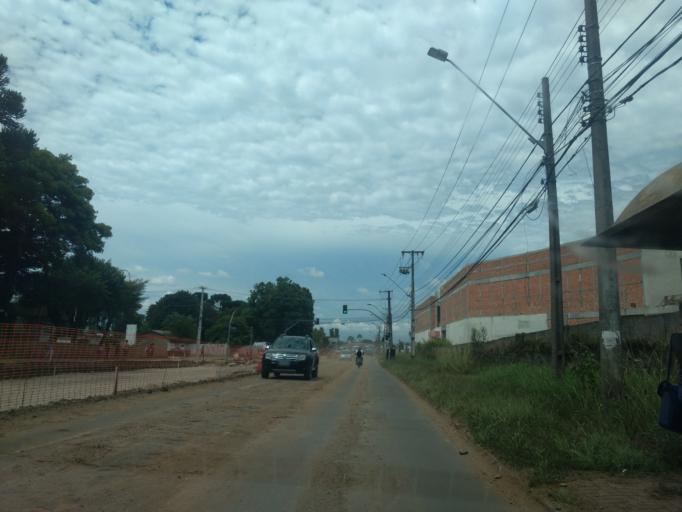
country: BR
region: Parana
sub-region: Pinhais
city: Pinhais
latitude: -25.4273
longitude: -49.2147
